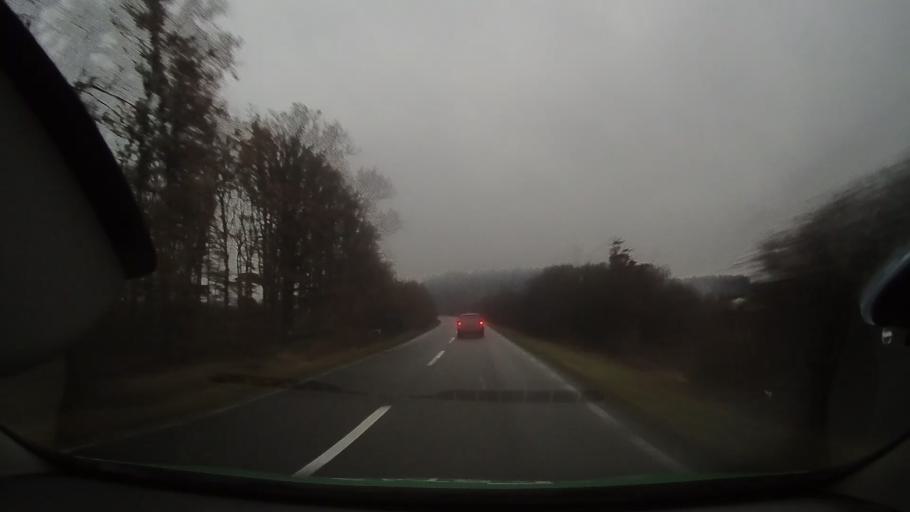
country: RO
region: Arad
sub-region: Comuna Beliu
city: Beliu
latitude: 46.5272
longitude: 21.9541
